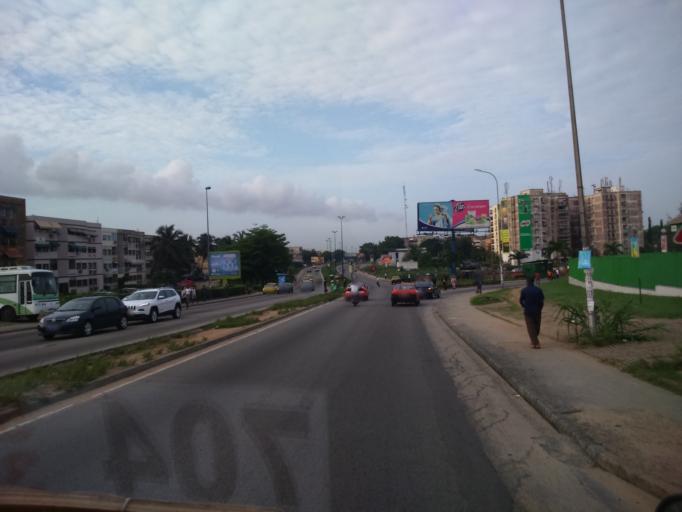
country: CI
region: Lagunes
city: Abobo
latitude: 5.3734
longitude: -3.9985
